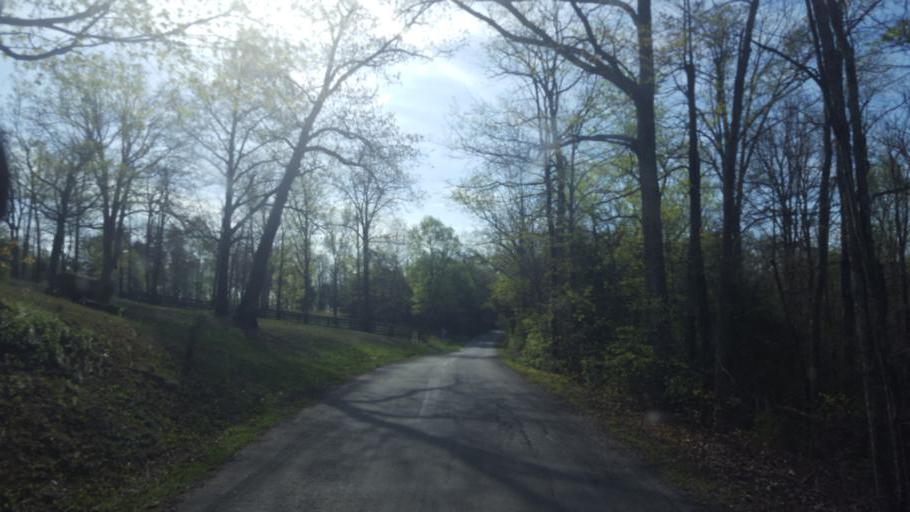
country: US
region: Kentucky
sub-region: Hart County
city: Munfordville
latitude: 37.3269
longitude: -86.0977
